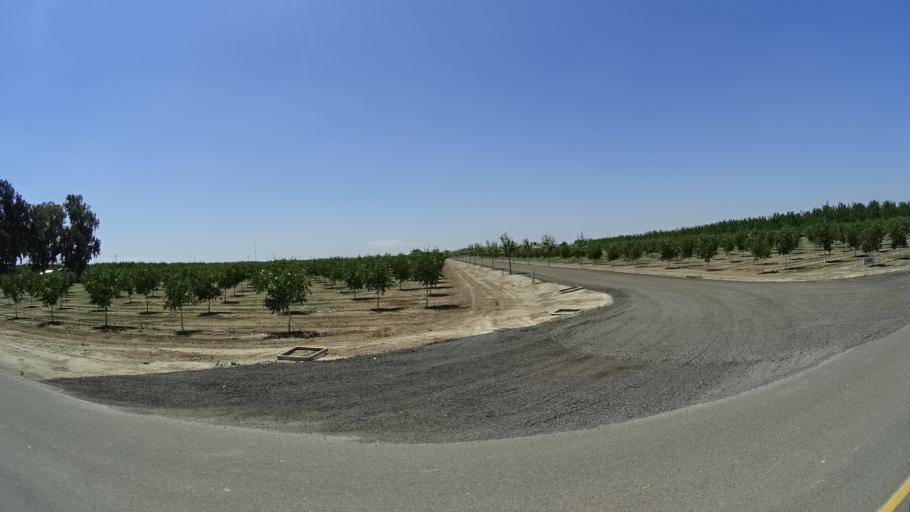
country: US
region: California
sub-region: Kings County
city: Lucerne
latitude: 36.4072
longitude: -119.6548
